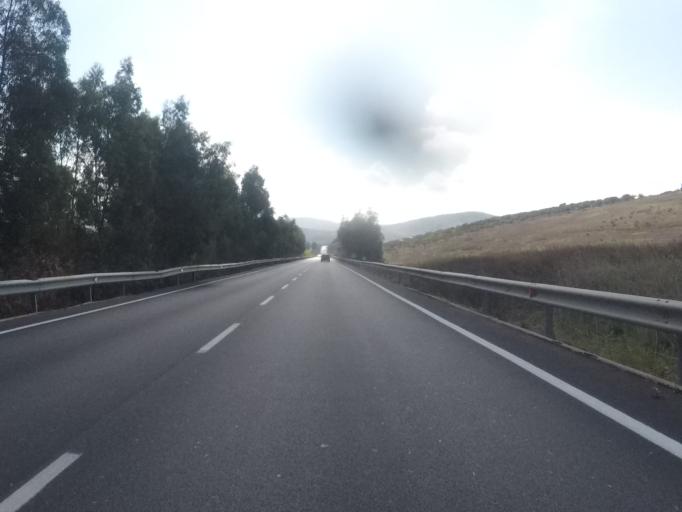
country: IT
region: Sicily
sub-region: Agrigento
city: Ribera
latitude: 37.4318
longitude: 13.2902
